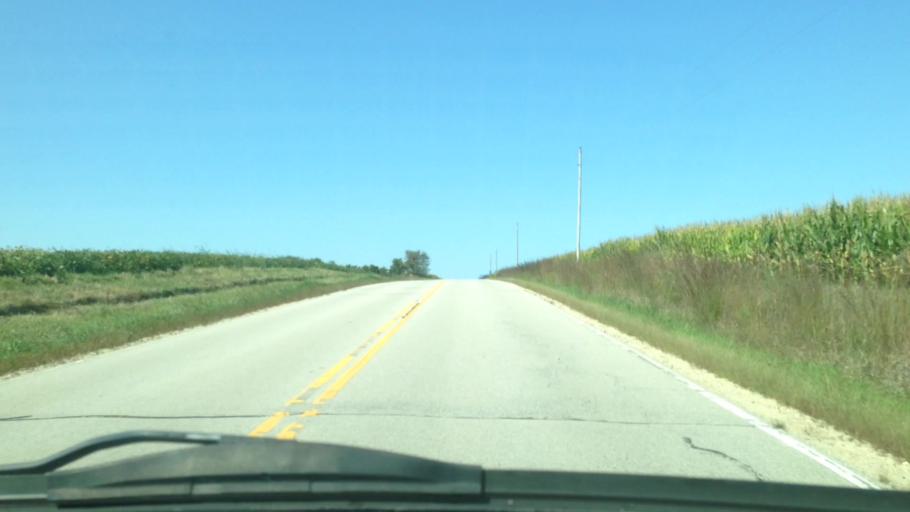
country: US
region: Minnesota
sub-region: Fillmore County
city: Rushford
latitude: 43.7122
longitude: -91.7703
